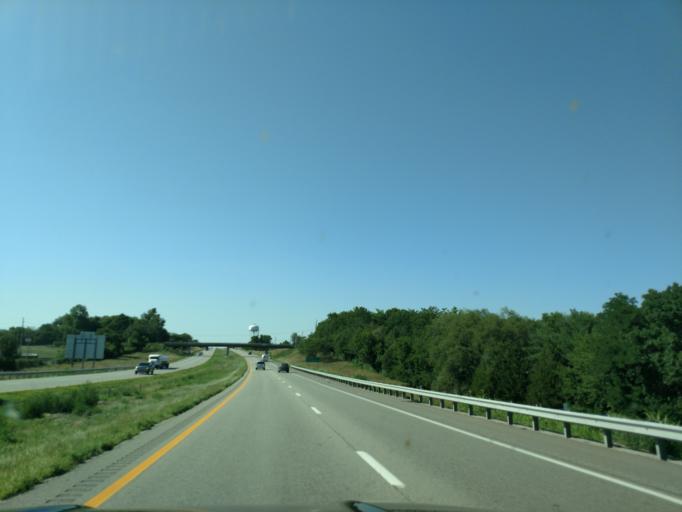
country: US
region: Missouri
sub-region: Andrew County
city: Country Club Village
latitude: 39.7895
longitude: -94.7955
